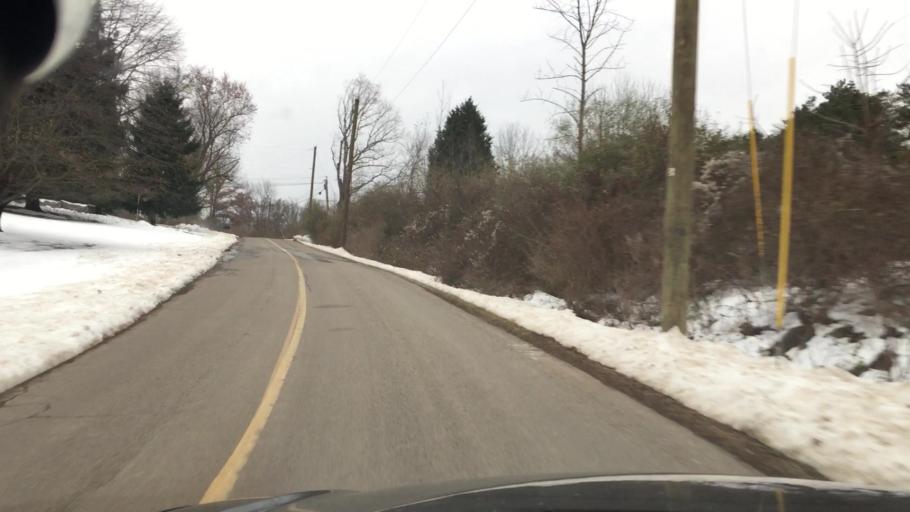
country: US
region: Pennsylvania
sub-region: Luzerne County
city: Conyngham
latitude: 41.0041
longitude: -76.1400
